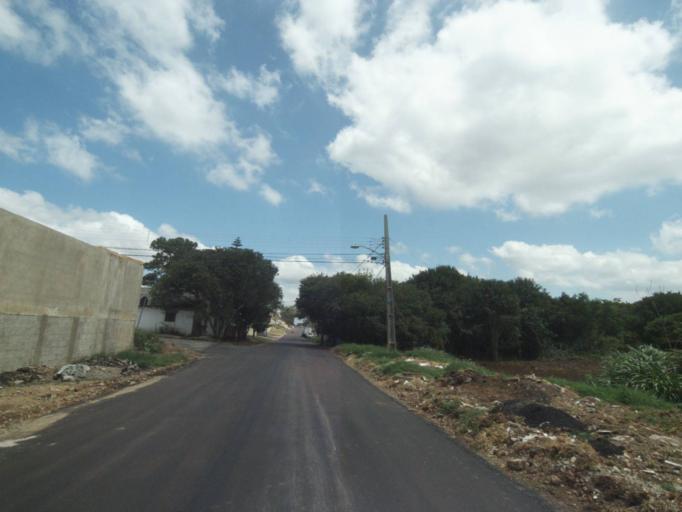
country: BR
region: Parana
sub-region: Curitiba
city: Curitiba
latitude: -25.5084
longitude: -49.3063
